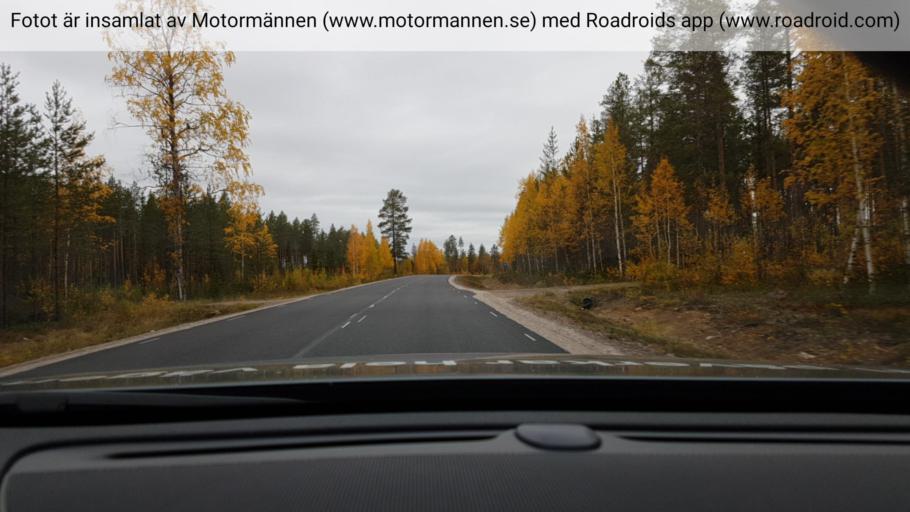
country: SE
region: Norrbotten
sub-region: Overkalix Kommun
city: OEverkalix
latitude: 66.4034
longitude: 22.8081
